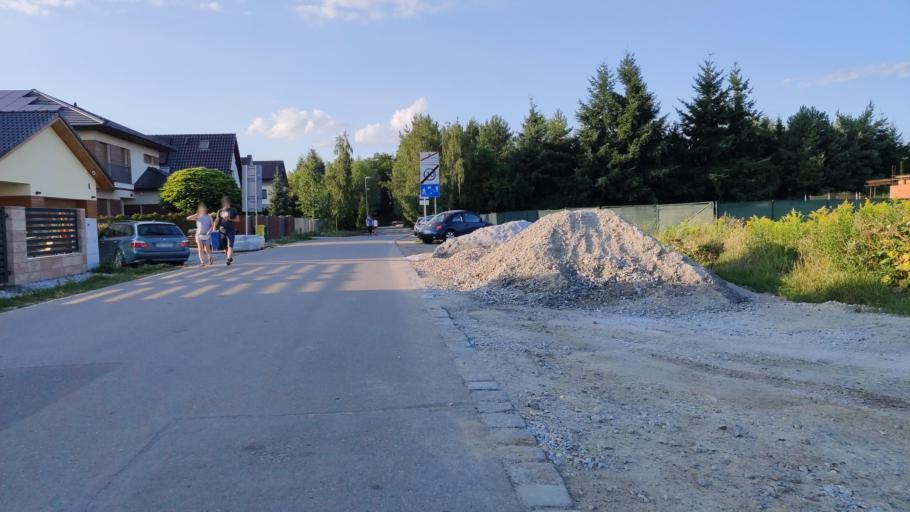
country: PL
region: Lower Silesian Voivodeship
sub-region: Powiat wroclawski
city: Zerniki Wroclawskie
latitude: 51.0540
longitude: 17.0661
